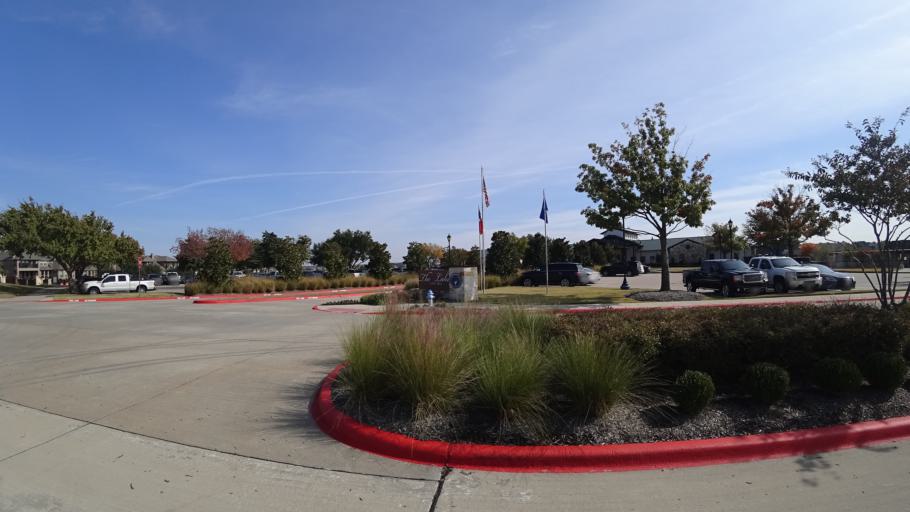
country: US
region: Texas
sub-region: Denton County
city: The Colony
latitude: 33.0420
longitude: -96.9066
